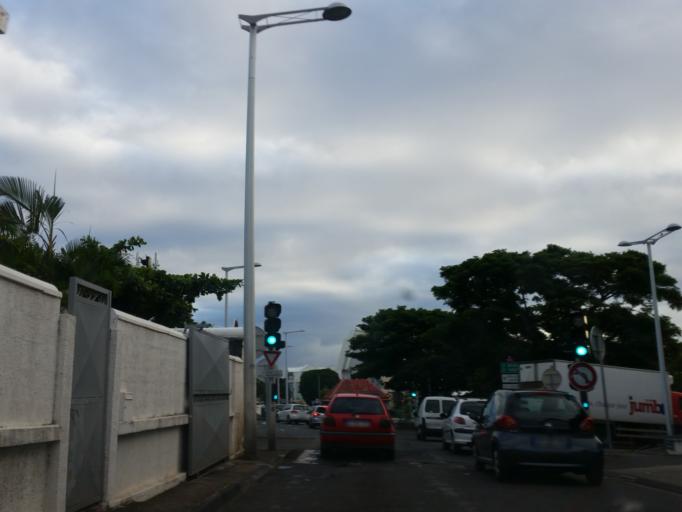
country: RE
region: Reunion
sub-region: Reunion
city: Saint-Denis
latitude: -20.8890
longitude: 55.4463
